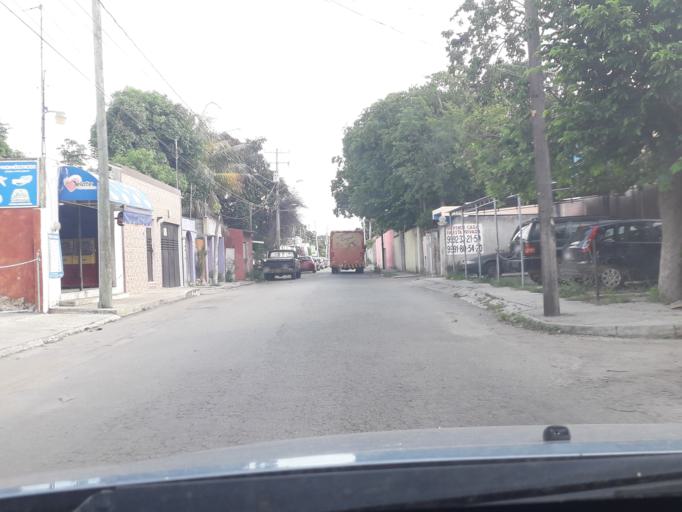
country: MX
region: Yucatan
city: Merida
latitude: 21.0117
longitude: -89.6364
